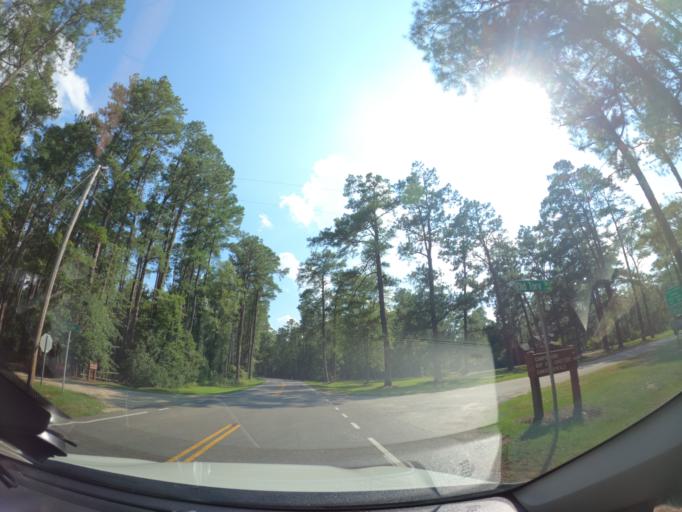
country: US
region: South Carolina
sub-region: Barnwell County
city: Williston
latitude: 33.5501
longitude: -81.4889
